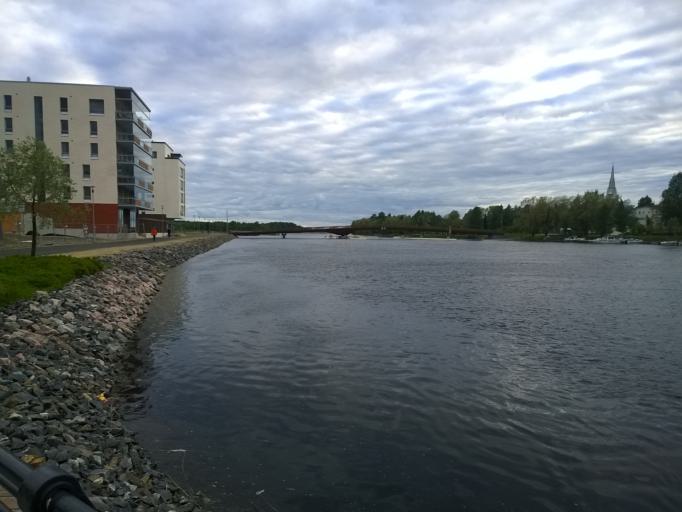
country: FI
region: North Karelia
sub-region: Joensuu
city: Joensuu
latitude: 62.5945
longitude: 29.7630
